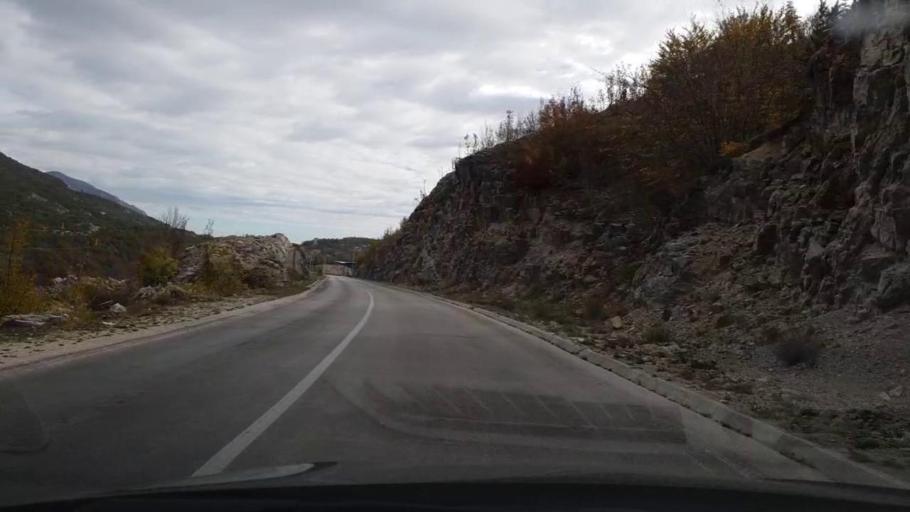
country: ME
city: Igalo
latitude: 42.5606
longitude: 18.4443
